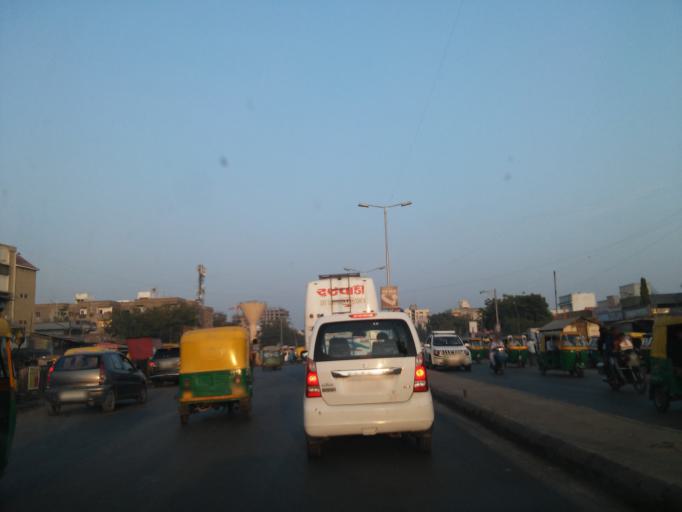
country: IN
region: Gujarat
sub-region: Ahmadabad
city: Sarkhej
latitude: 22.9942
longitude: 72.5282
